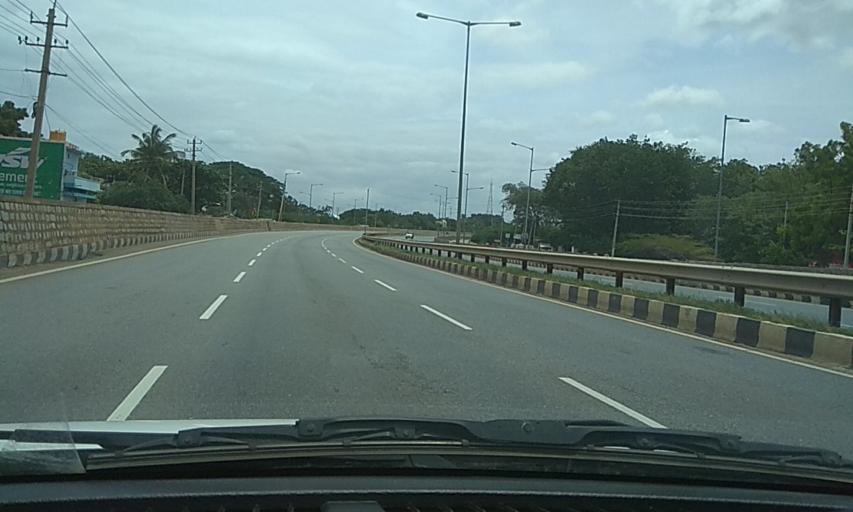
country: IN
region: Karnataka
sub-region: Chitradurga
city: Hiriyur
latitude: 13.9582
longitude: 76.6161
